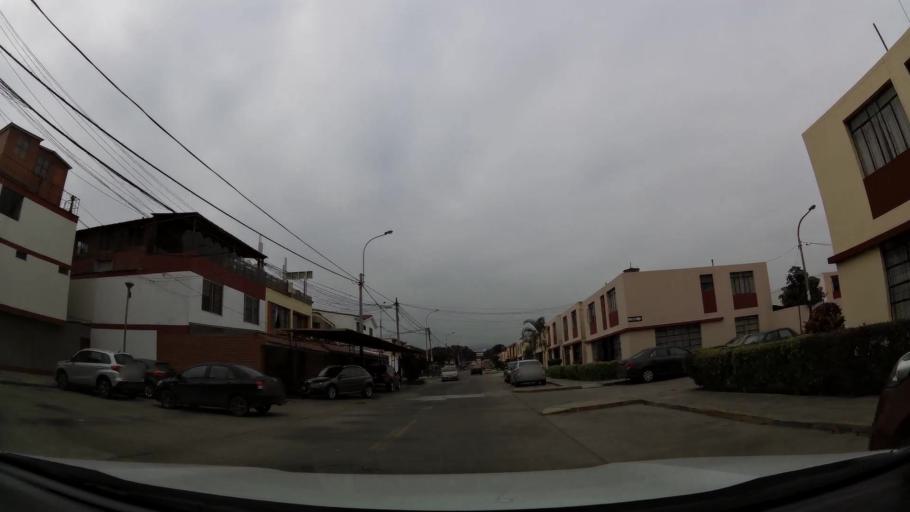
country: PE
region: Lima
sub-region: Lima
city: Surco
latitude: -12.1573
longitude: -77.0215
